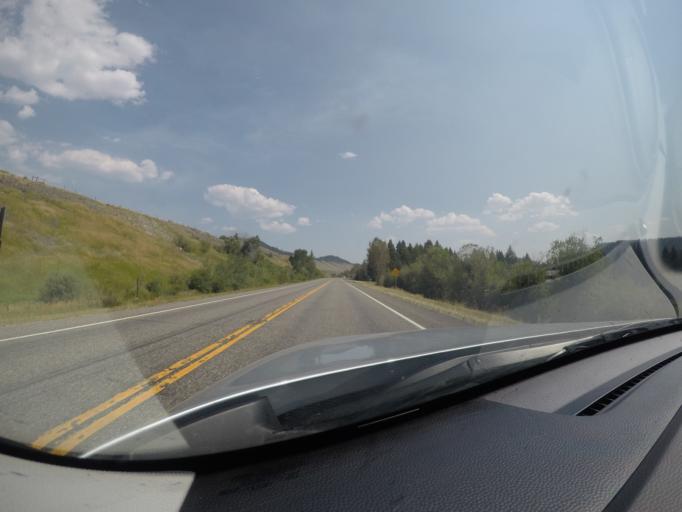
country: US
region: Montana
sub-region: Gallatin County
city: Big Sky
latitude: 44.8999
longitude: -111.5895
